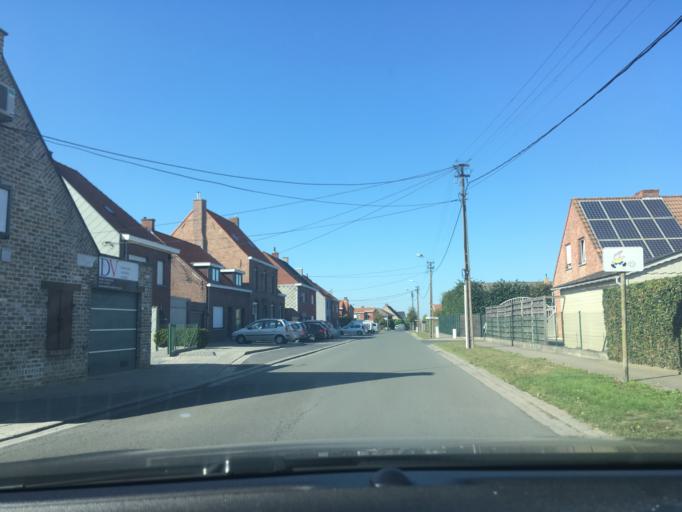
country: BE
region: Flanders
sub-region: Provincie West-Vlaanderen
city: Ledegem
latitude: 50.8691
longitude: 3.1445
